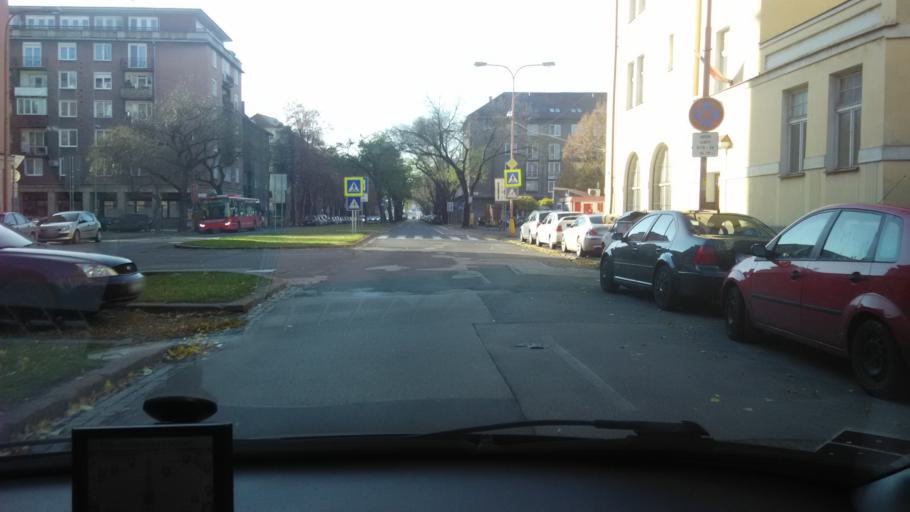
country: SK
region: Bratislavsky
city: Bratislava
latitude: 48.1501
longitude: 17.1347
